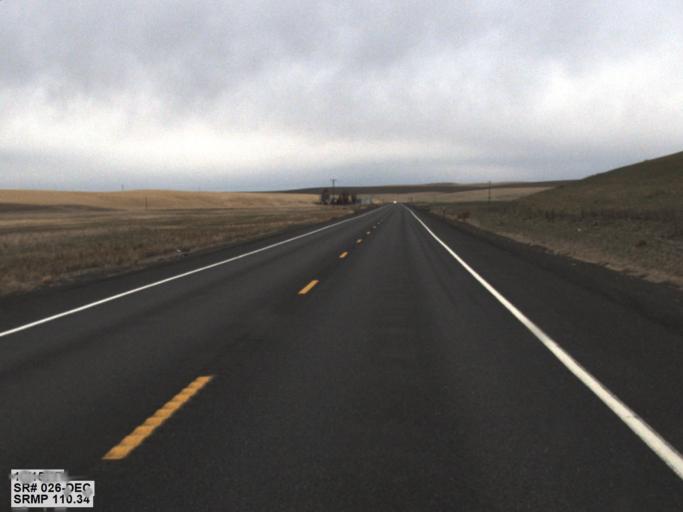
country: US
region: Washington
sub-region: Garfield County
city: Pomeroy
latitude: 46.8069
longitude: -117.7873
